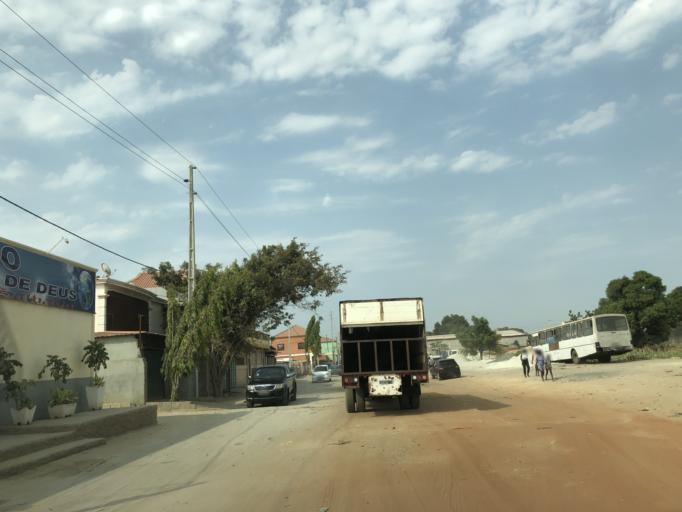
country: AO
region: Luanda
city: Luanda
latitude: -8.8953
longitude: 13.3522
